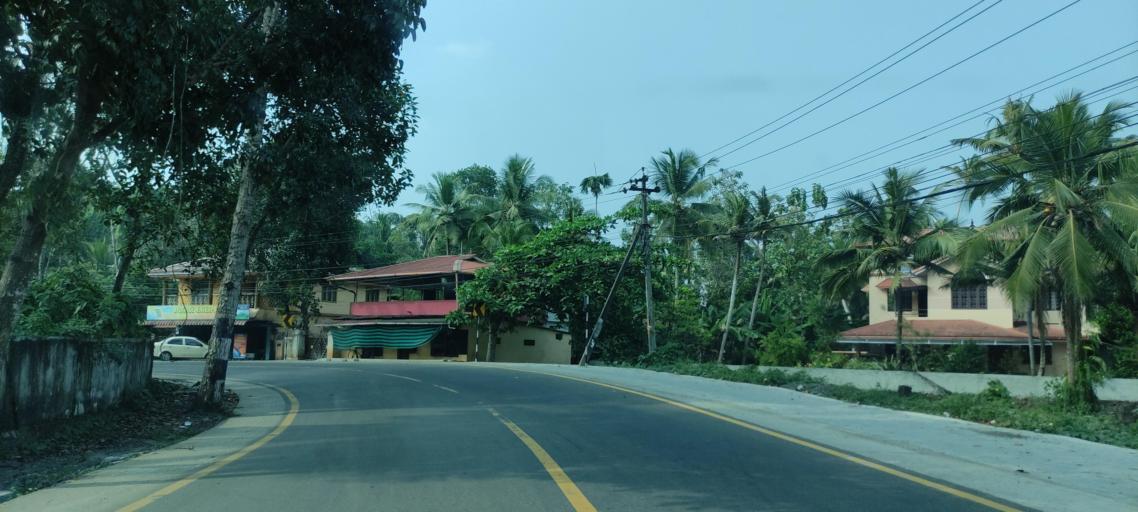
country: IN
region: Kerala
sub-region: Pattanamtitta
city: Tiruvalla
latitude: 9.3687
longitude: 76.5424
